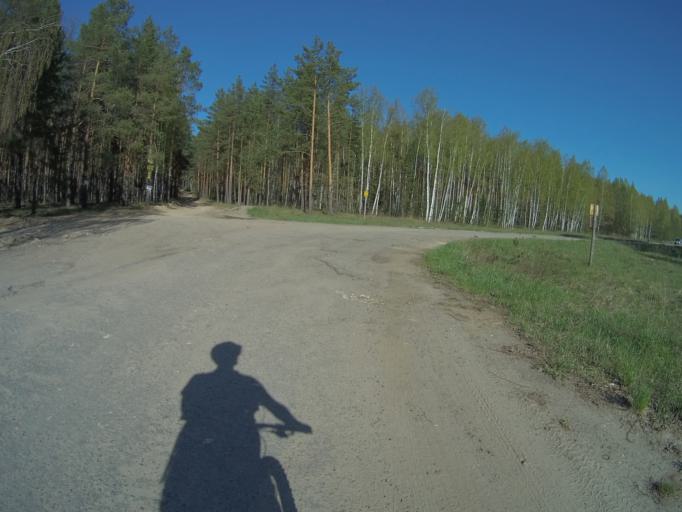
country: RU
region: Vladimir
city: Sudogda
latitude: 56.1484
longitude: 40.8582
